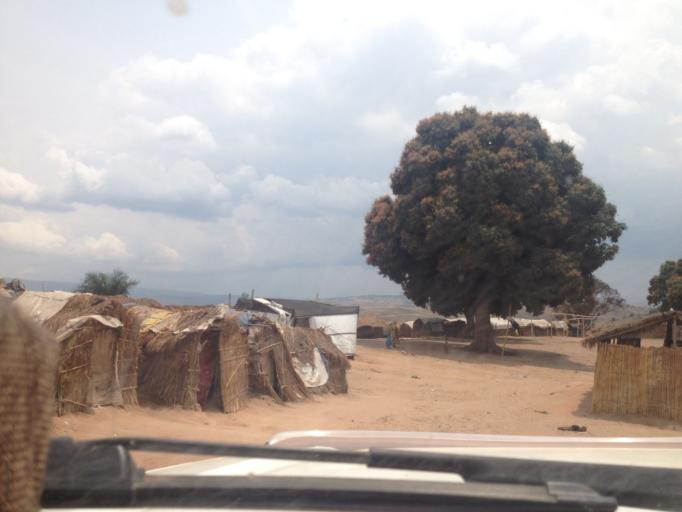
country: CD
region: Katanga
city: Kalemie
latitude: -5.9279
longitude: 29.1738
